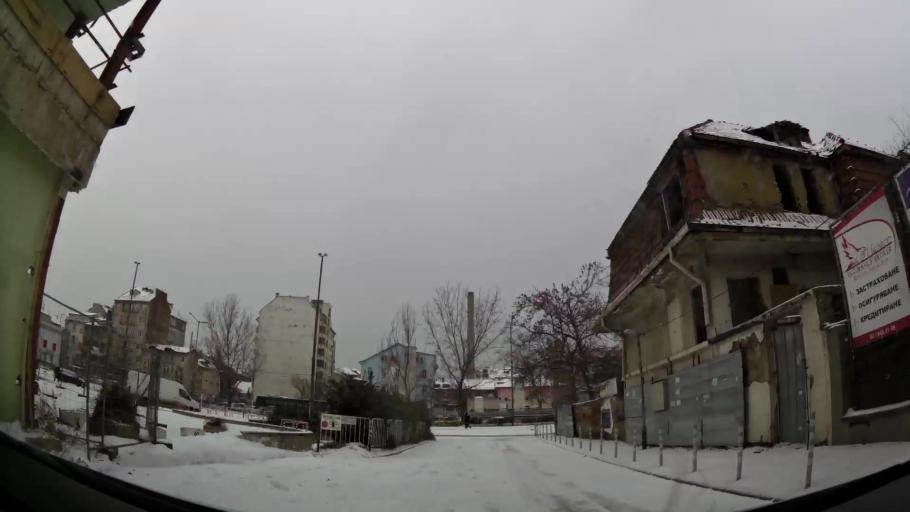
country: BG
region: Sofia-Capital
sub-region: Stolichna Obshtina
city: Sofia
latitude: 42.6918
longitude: 23.3082
